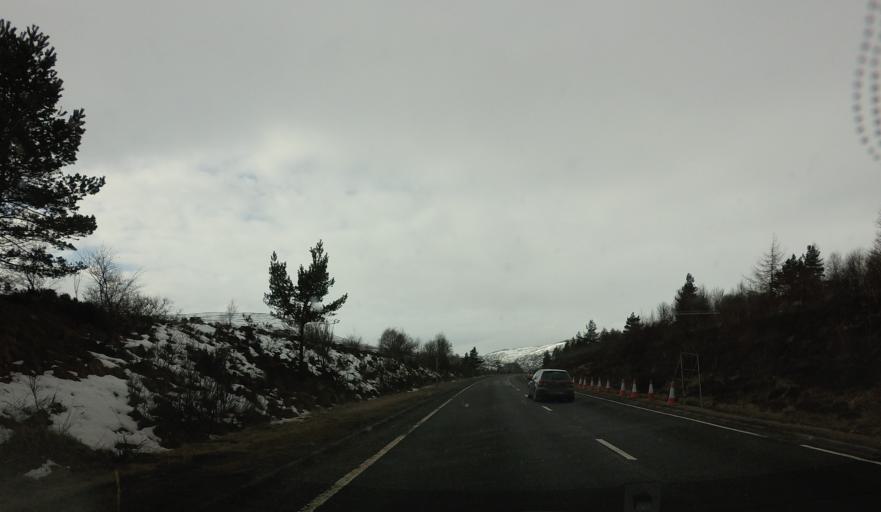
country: GB
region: Scotland
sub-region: Highland
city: Kingussie
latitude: 56.8106
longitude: -4.1153
